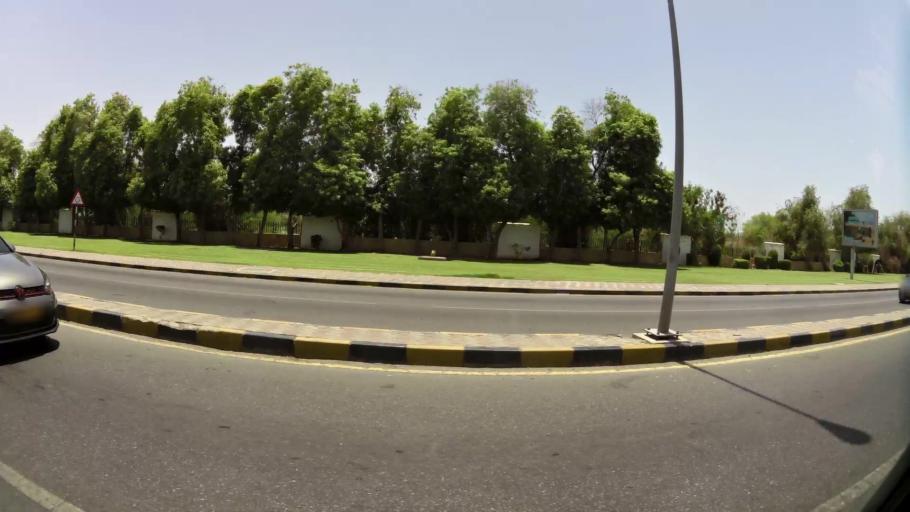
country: OM
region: Muhafazat Masqat
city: Muscat
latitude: 23.6184
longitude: 58.4950
